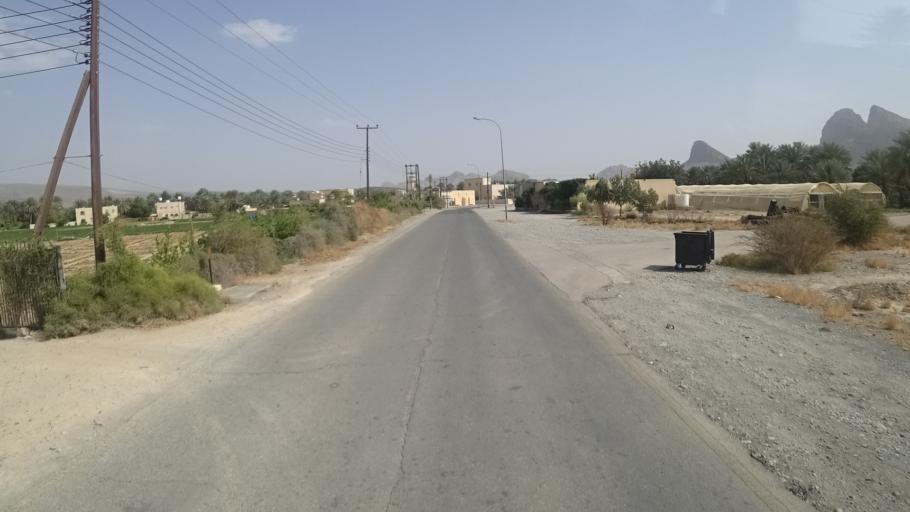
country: OM
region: Muhafazat ad Dakhiliyah
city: Bahla'
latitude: 23.1036
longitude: 57.3007
